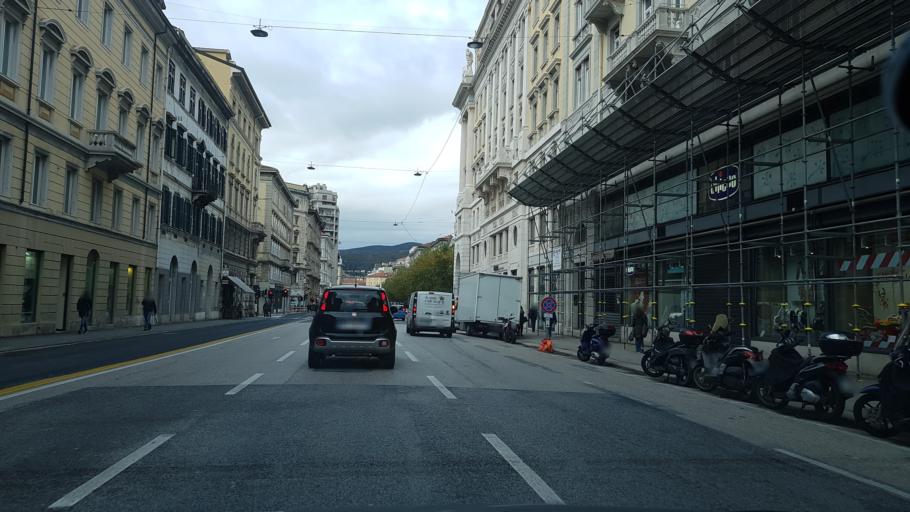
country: IT
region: Friuli Venezia Giulia
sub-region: Provincia di Trieste
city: Trieste
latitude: 45.6507
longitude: 13.7775
